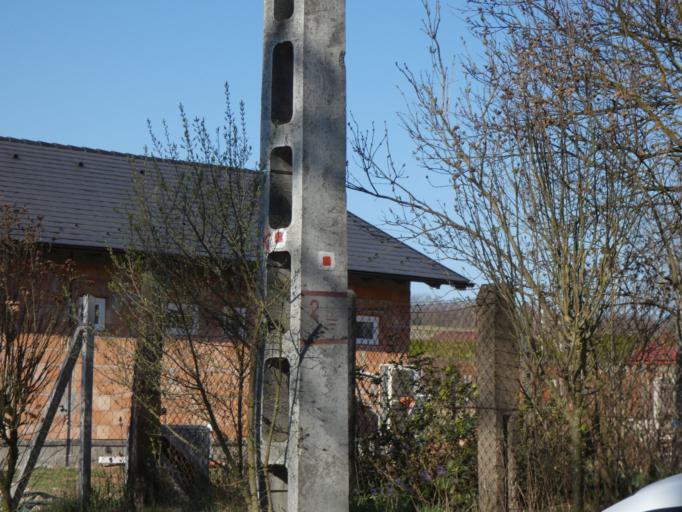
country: HU
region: Pest
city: Isaszeg
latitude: 47.5485
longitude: 19.3755
